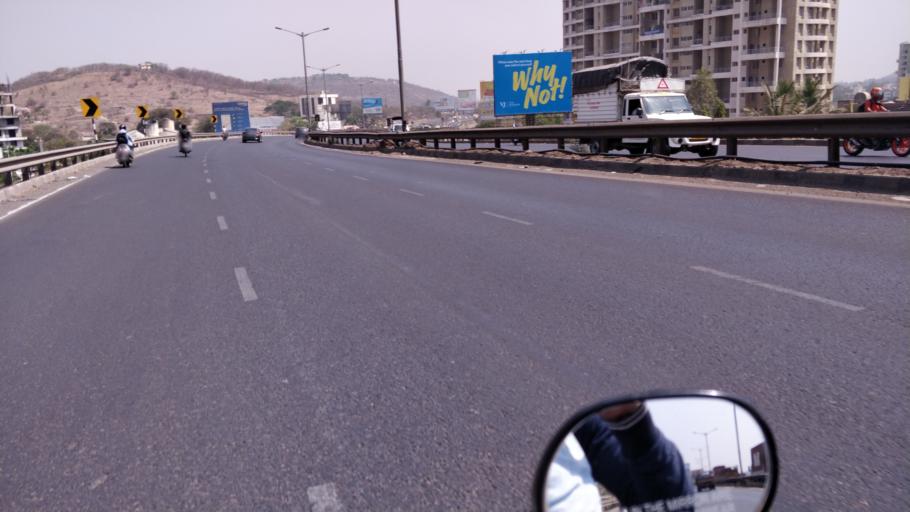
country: IN
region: Maharashtra
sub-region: Pune Division
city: Kharakvasla
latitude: 18.5211
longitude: 73.7693
